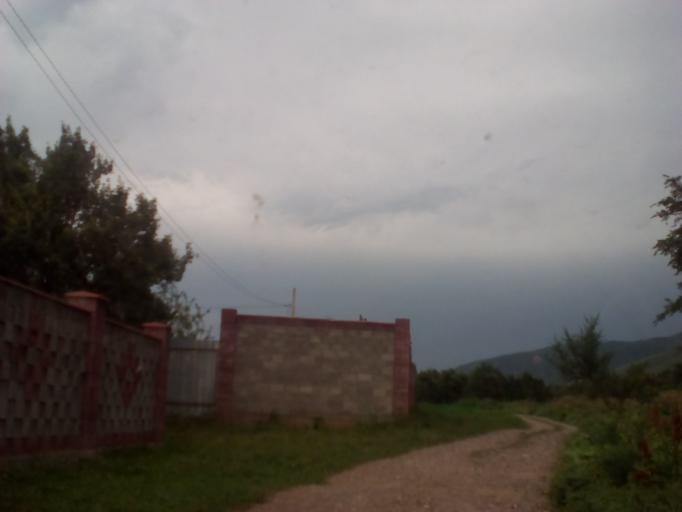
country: KZ
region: Almaty Oblysy
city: Burunday
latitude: 43.1580
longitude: 76.3987
